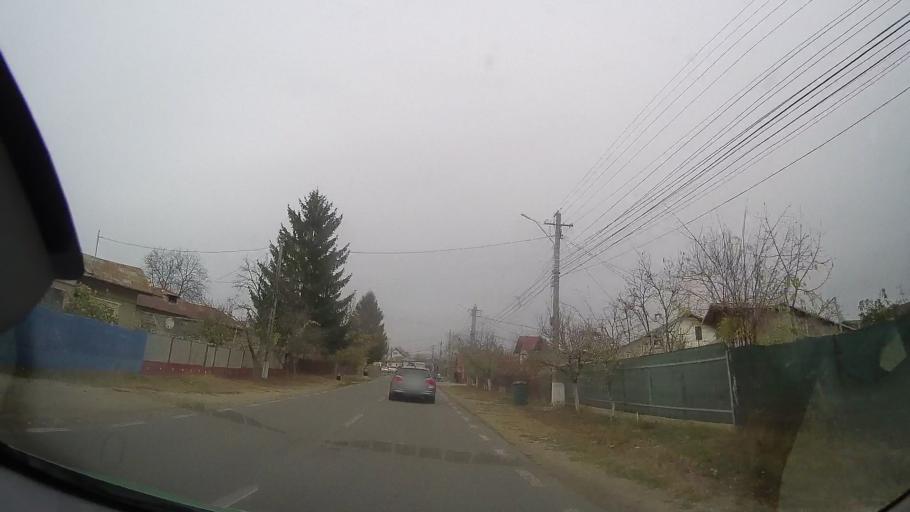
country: RO
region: Prahova
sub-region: Oras Baicoi
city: Liliesti
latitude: 45.0297
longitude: 25.8869
